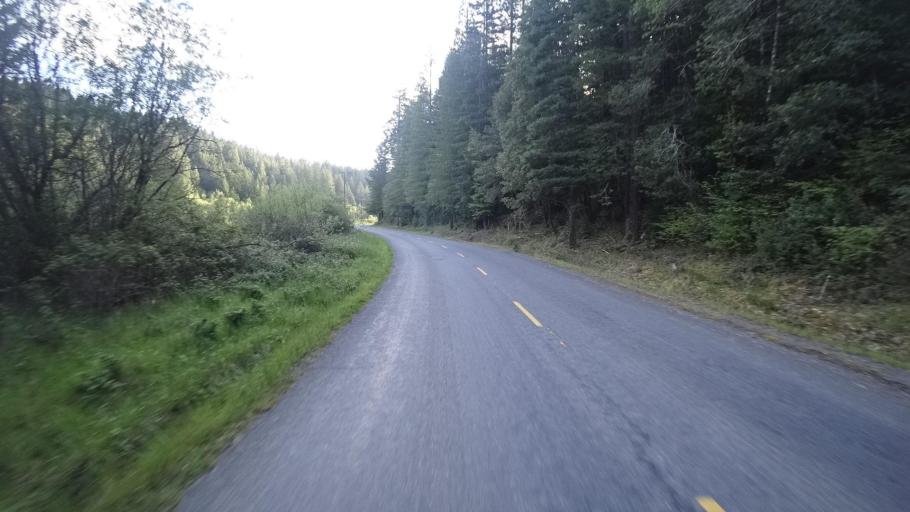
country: US
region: California
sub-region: Humboldt County
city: Rio Dell
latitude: 40.3496
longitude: -124.0185
